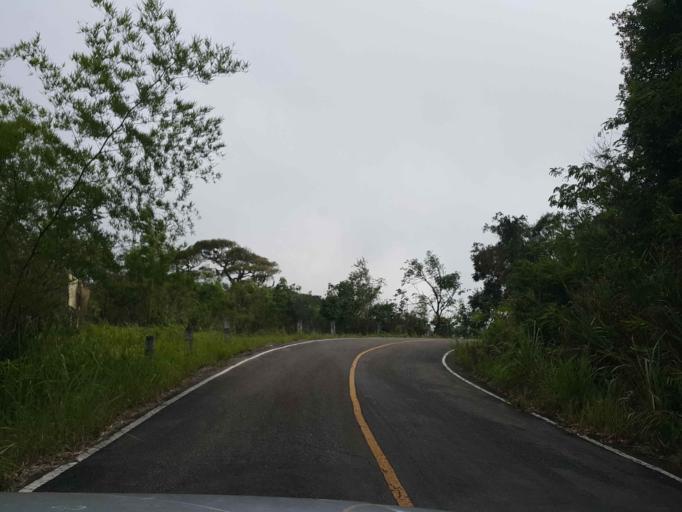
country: TH
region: Tak
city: Tak
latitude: 16.7909
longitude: 98.9222
